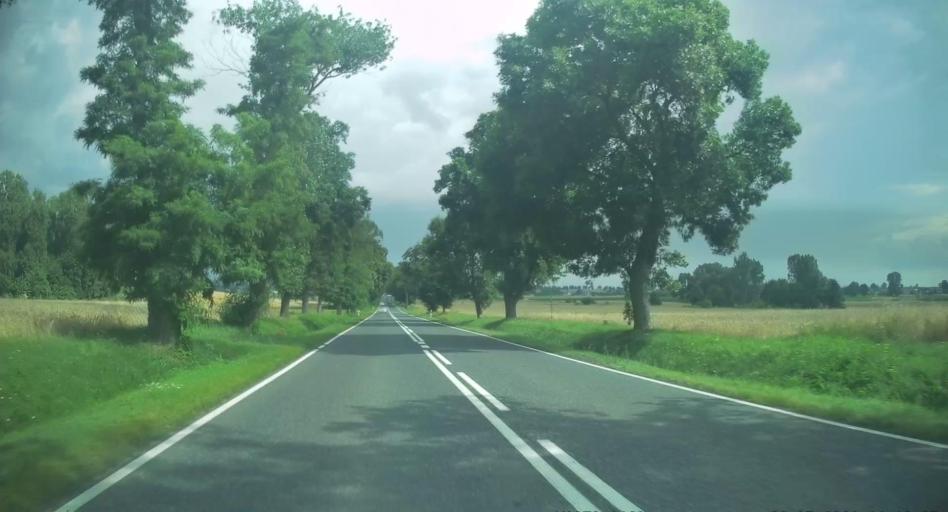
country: PL
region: Lodz Voivodeship
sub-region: Powiat skierniewicki
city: Gluchow
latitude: 51.7860
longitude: 20.0525
